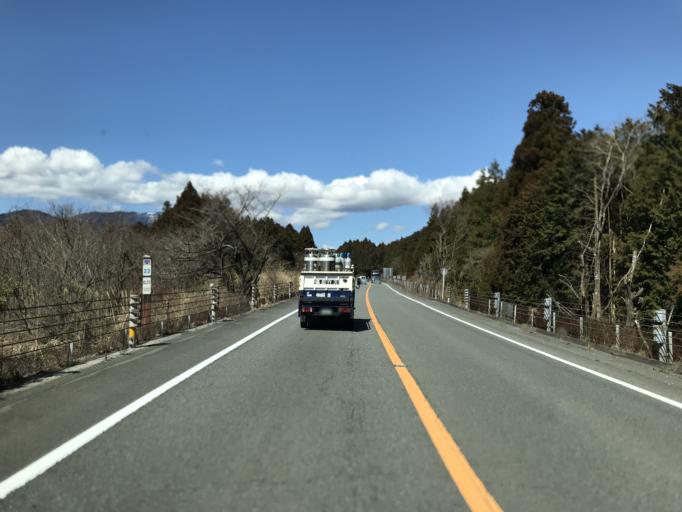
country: JP
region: Shizuoka
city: Fujinomiya
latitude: 35.3214
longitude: 138.5905
